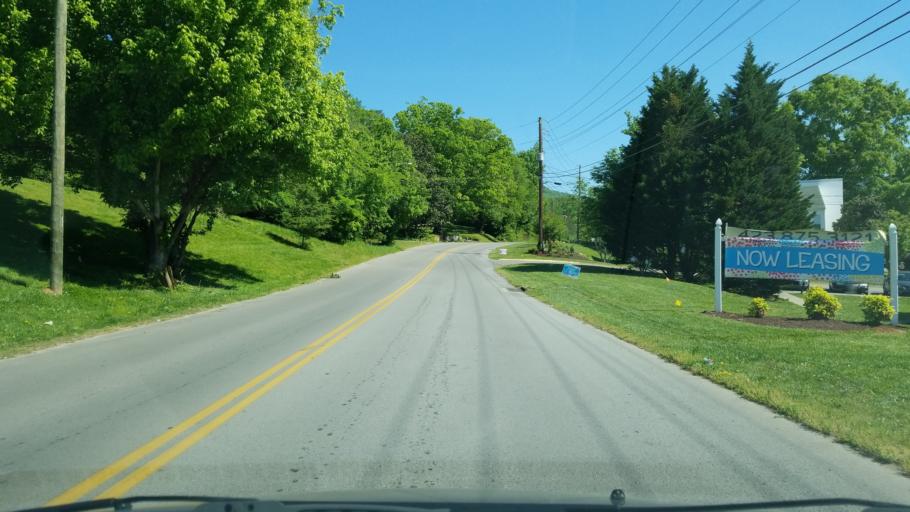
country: US
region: Tennessee
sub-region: Hamilton County
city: Red Bank
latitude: 35.1278
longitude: -85.3098
